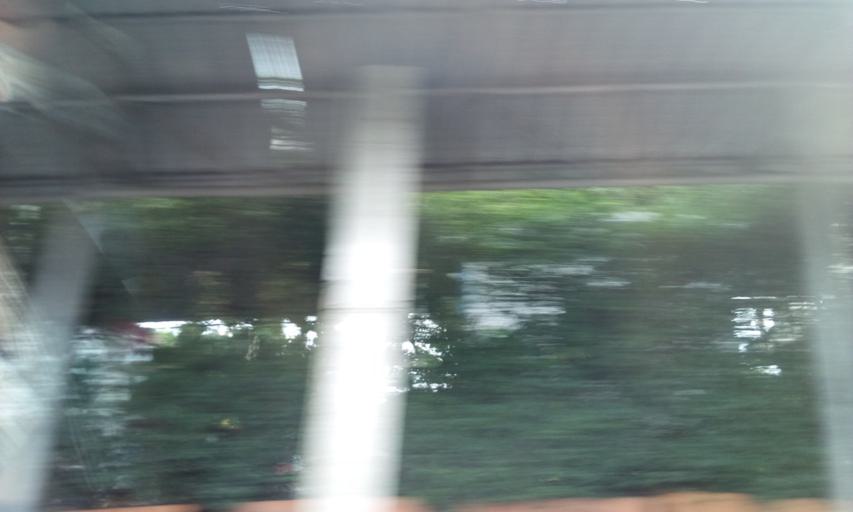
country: TH
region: Bangkok
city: Don Mueang
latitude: 13.9380
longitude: 100.5452
